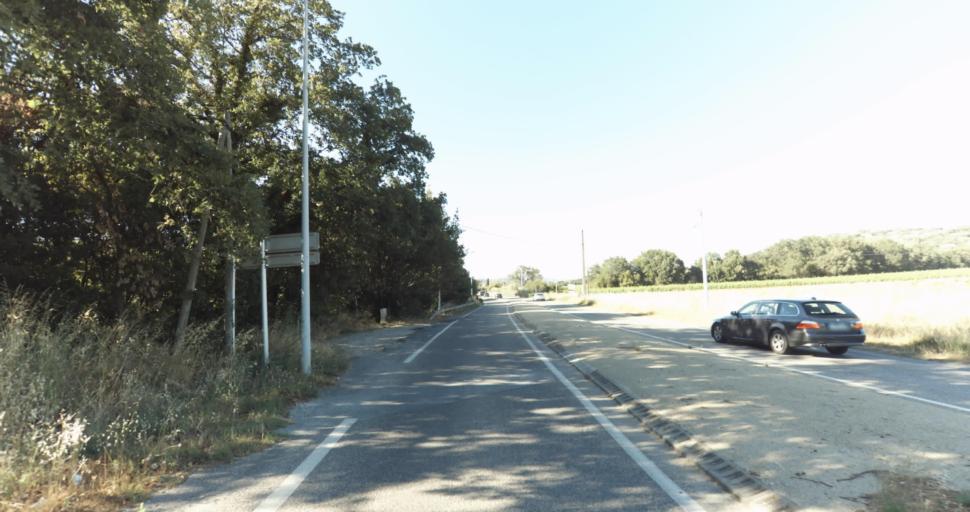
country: FR
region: Provence-Alpes-Cote d'Azur
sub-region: Departement du Var
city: Gassin
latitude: 43.2515
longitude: 6.5921
